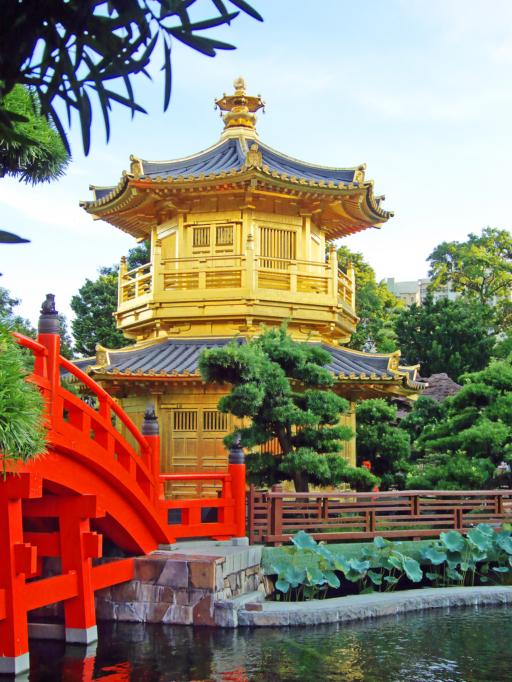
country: HK
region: Wong Tai Sin
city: Wong Tai Sin
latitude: 22.3394
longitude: 114.2044
